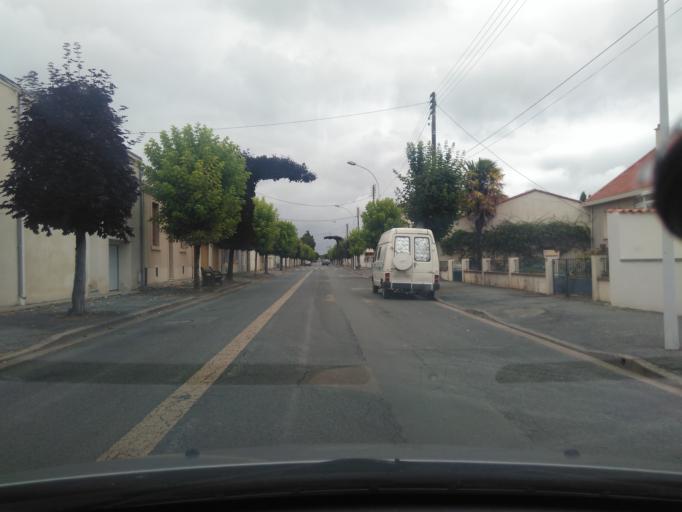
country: FR
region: Pays de la Loire
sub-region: Departement de la Vendee
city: Lucon
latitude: 46.4614
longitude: -1.1701
